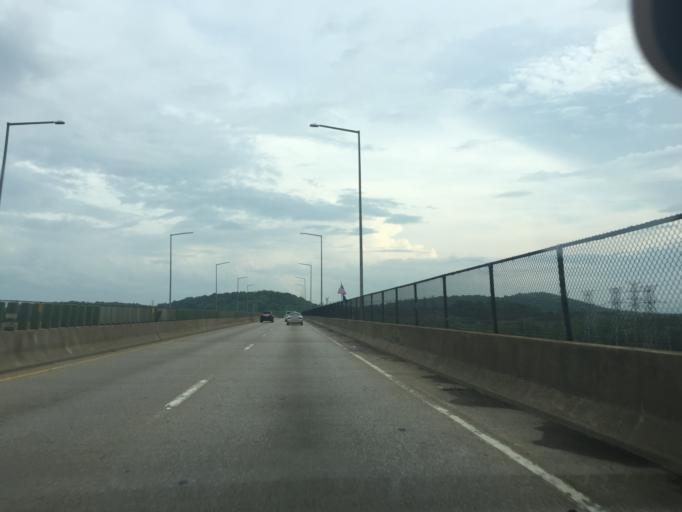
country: US
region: Tennessee
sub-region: Hamilton County
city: East Chattanooga
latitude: 35.1038
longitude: -85.2292
